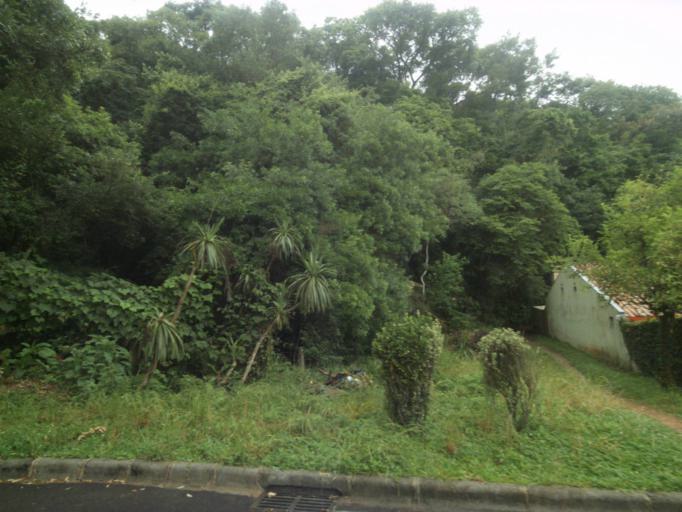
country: BR
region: Parana
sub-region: Curitiba
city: Curitiba
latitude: -25.4261
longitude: -49.3178
